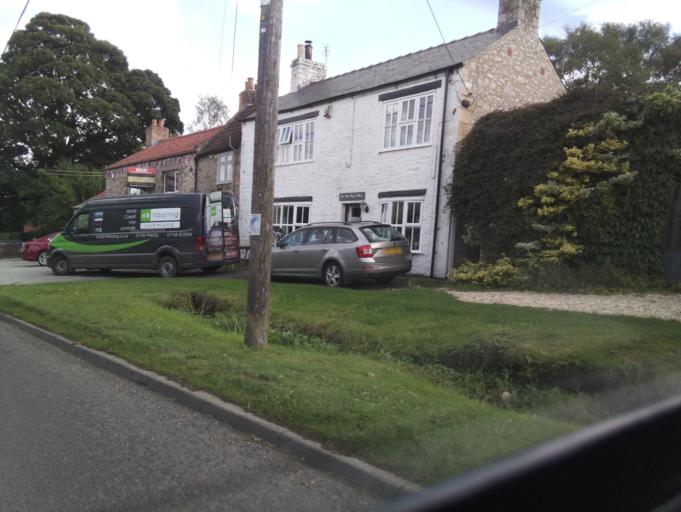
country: GB
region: England
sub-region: North Yorkshire
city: Catterick Garrison
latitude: 54.4177
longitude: -1.6955
